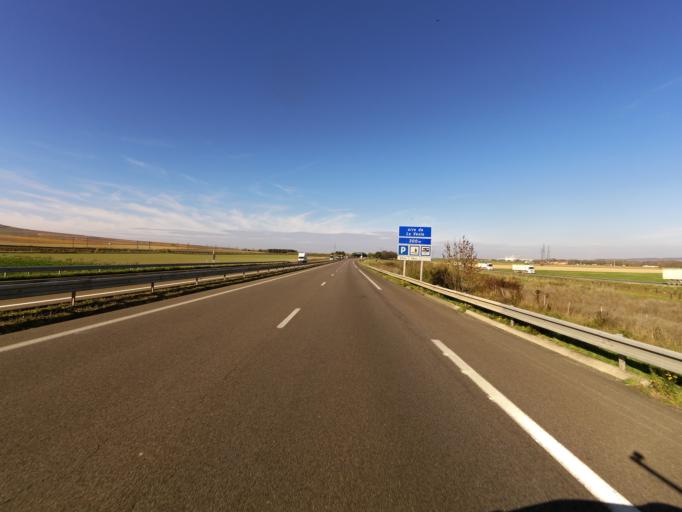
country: FR
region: Champagne-Ardenne
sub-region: Departement de la Marne
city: Verzy
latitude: 49.1715
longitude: 4.1731
